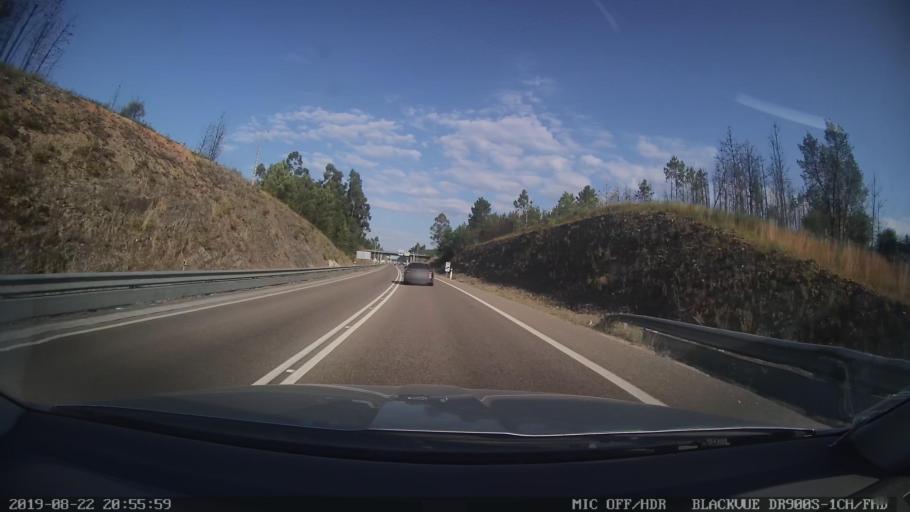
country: PT
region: Castelo Branco
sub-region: Serta
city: Serta
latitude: 39.7859
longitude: -8.0425
